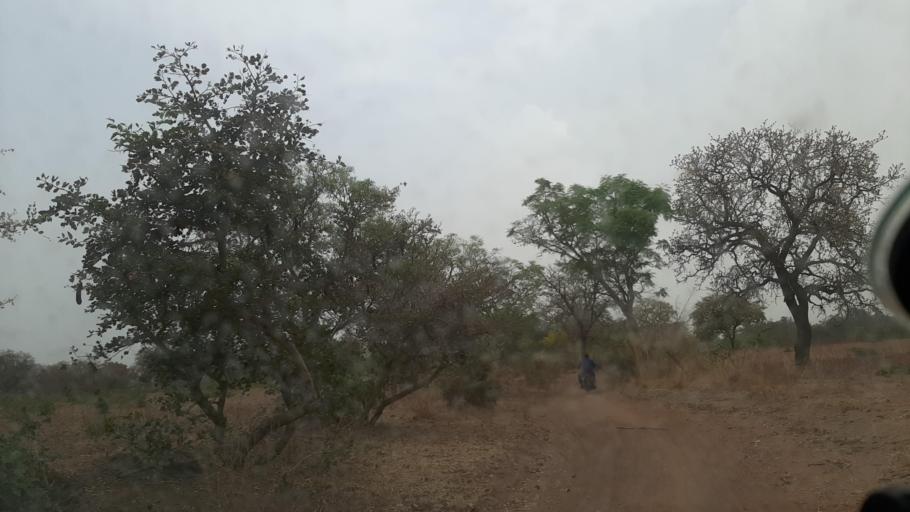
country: BF
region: Boucle du Mouhoun
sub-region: Province des Banwa
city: Salanso
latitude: 11.8552
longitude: -4.4302
